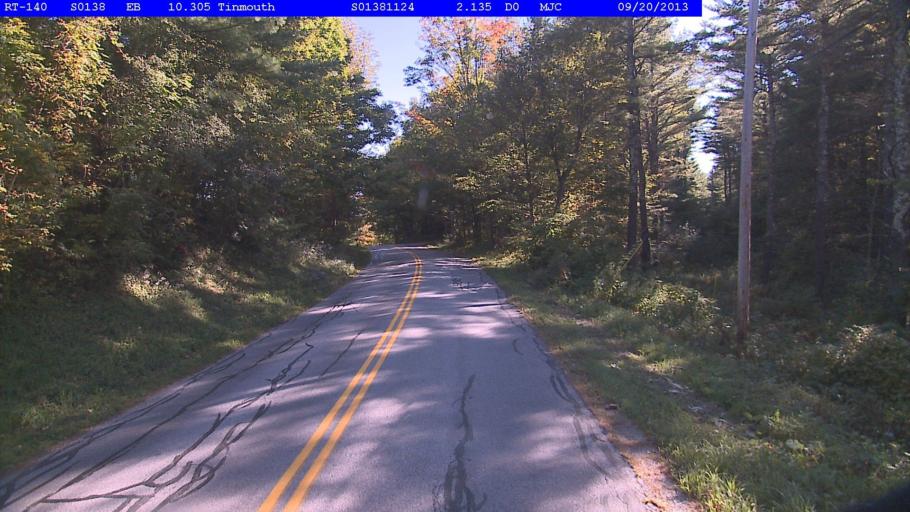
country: US
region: Vermont
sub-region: Rutland County
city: West Rutland
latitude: 43.4646
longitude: -73.0477
